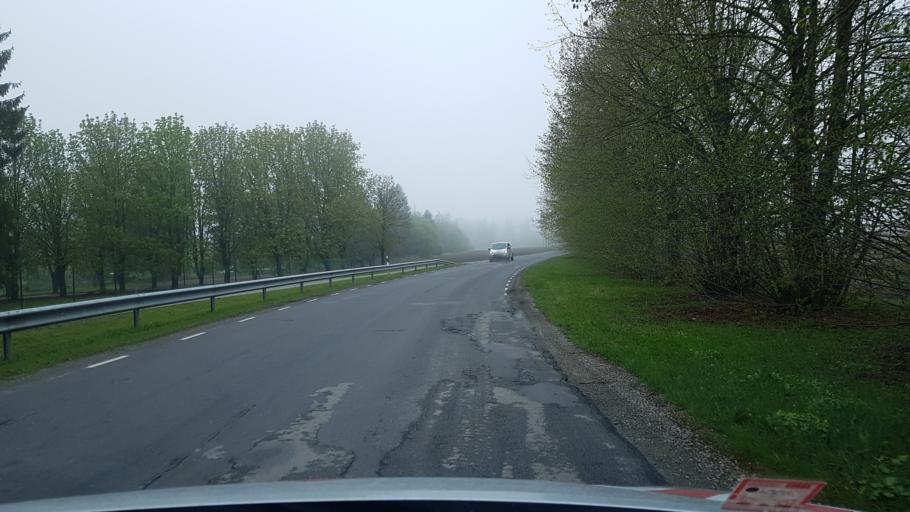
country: EE
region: Harju
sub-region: Joelaehtme vald
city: Loo
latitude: 59.4180
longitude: 24.9431
